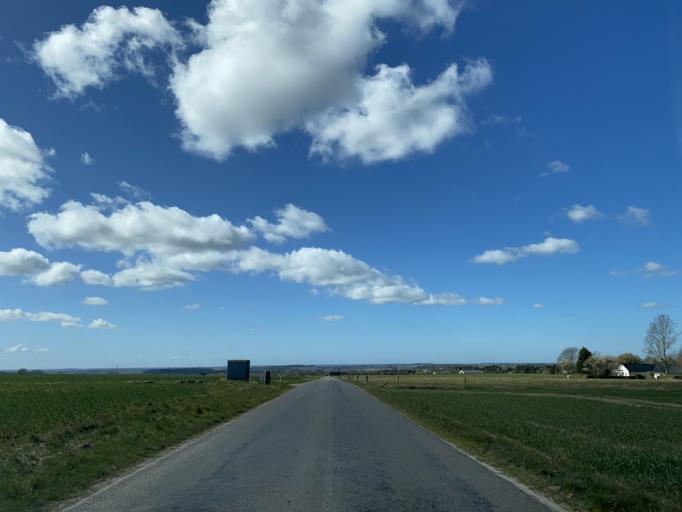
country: DK
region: Central Jutland
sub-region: Favrskov Kommune
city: Ulstrup
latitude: 56.3433
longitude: 9.8101
